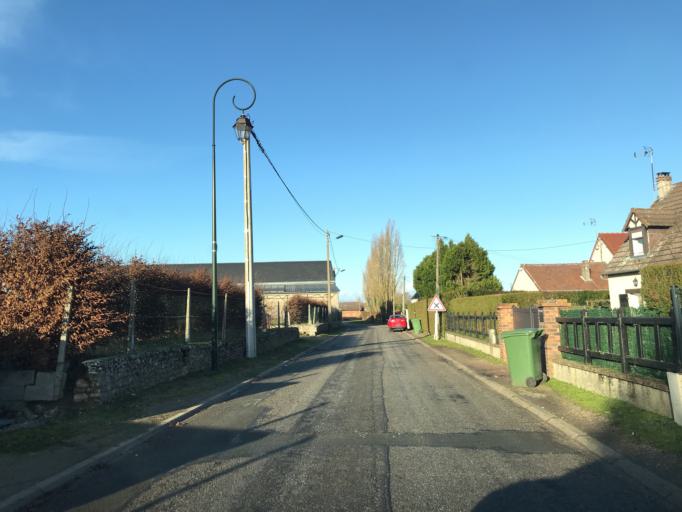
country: FR
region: Haute-Normandie
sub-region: Departement de l'Eure
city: Gravigny
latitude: 49.0807
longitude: 1.2230
